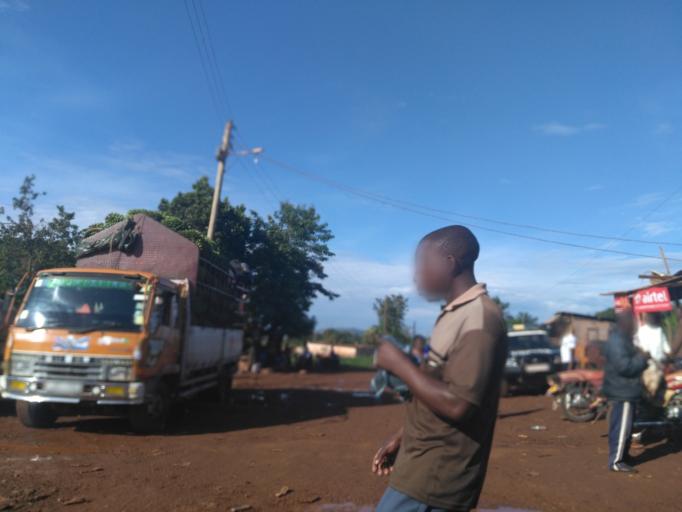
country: UG
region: Eastern Region
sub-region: Jinja District
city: Jinja
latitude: 0.4460
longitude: 33.1974
